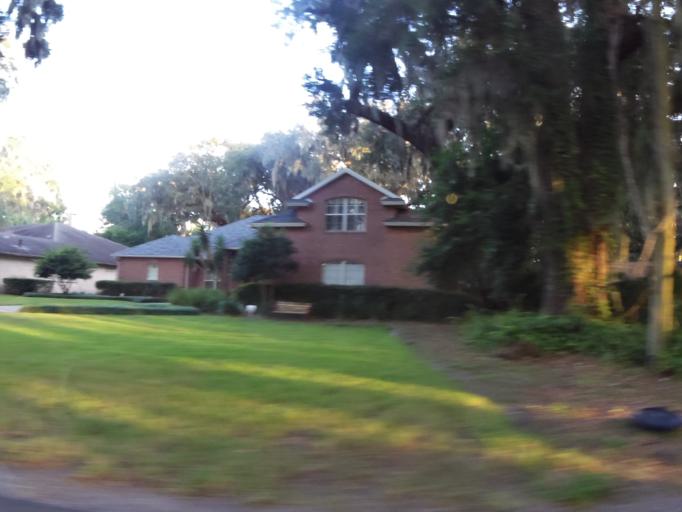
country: US
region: Florida
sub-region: Clay County
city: Orange Park
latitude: 30.2010
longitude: -81.6432
